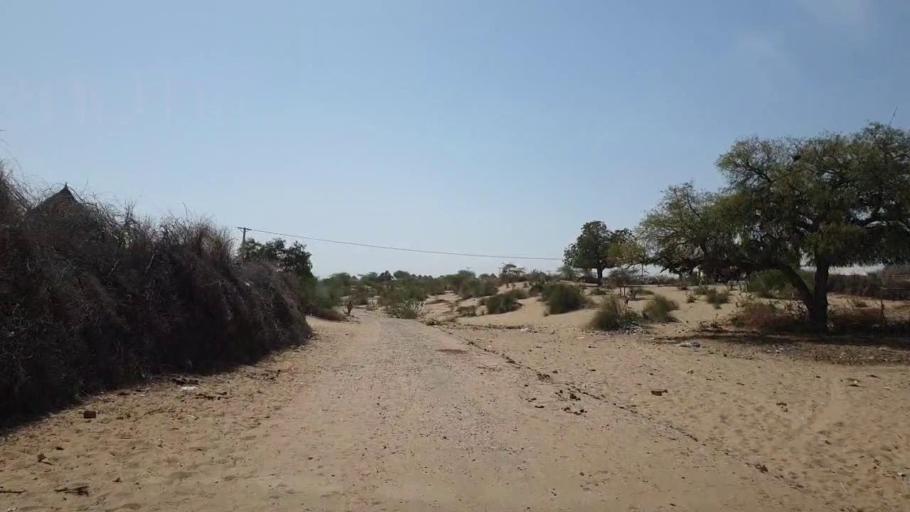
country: PK
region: Sindh
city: Umarkot
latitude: 25.1925
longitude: 69.8915
